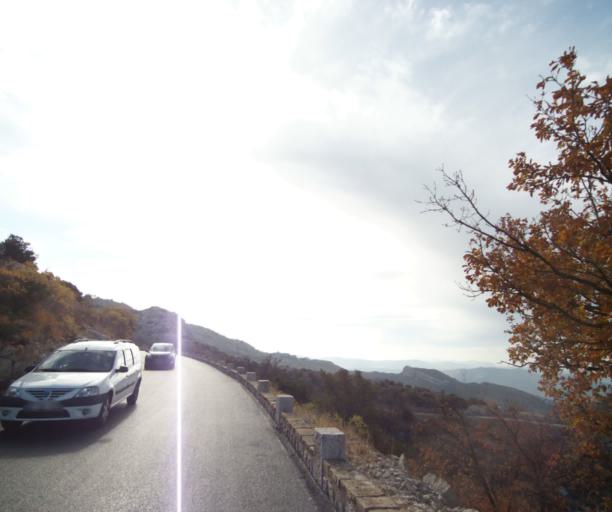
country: FR
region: Provence-Alpes-Cote d'Azur
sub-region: Departement des Bouches-du-Rhone
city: Gemenos
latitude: 43.3171
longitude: 5.6586
